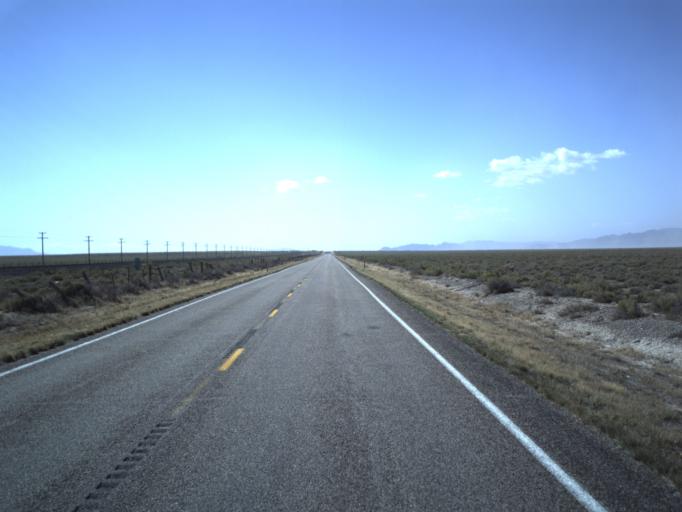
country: US
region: Utah
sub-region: Beaver County
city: Milford
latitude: 38.6983
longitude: -112.9732
